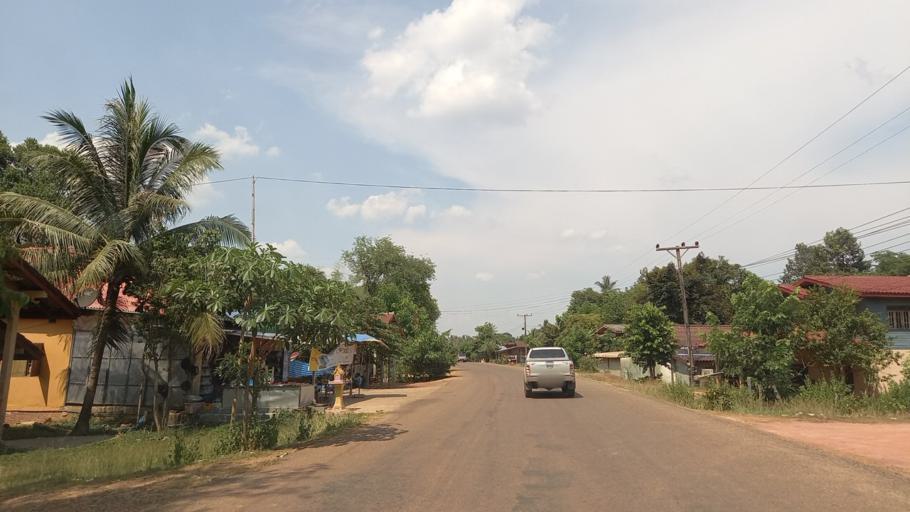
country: LA
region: Bolikhamxai
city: Muang Pakxan
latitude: 18.4055
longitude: 103.6979
